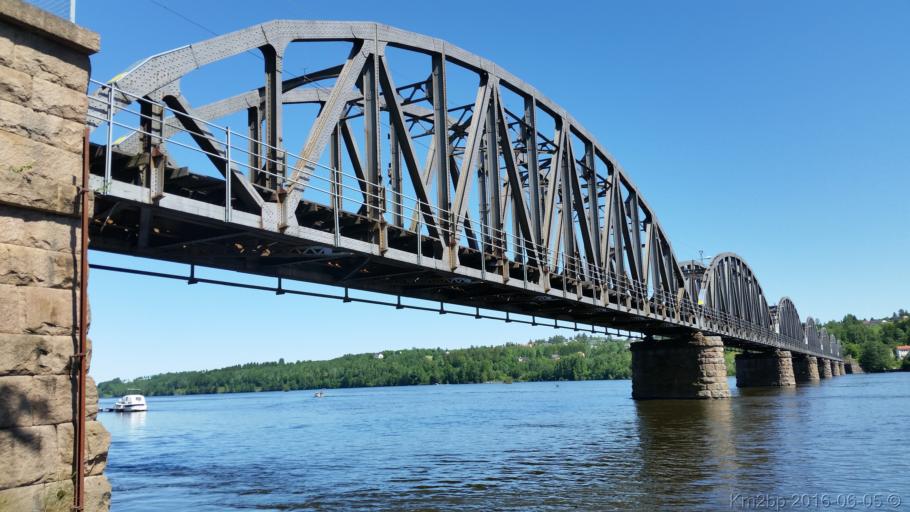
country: NO
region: Akershus
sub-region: Fet
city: Fetsund
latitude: 59.9280
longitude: 11.1667
